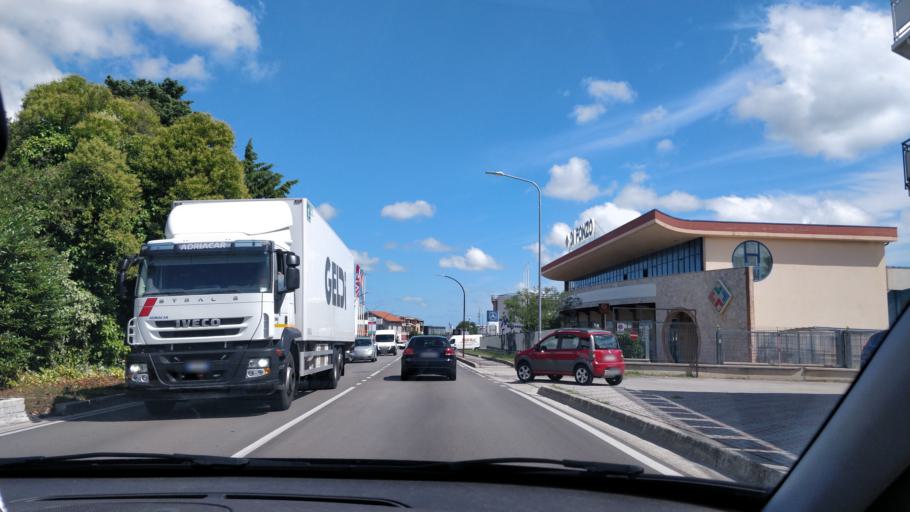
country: IT
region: Abruzzo
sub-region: Provincia di Chieti
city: Lanciano
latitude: 42.2376
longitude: 14.4092
